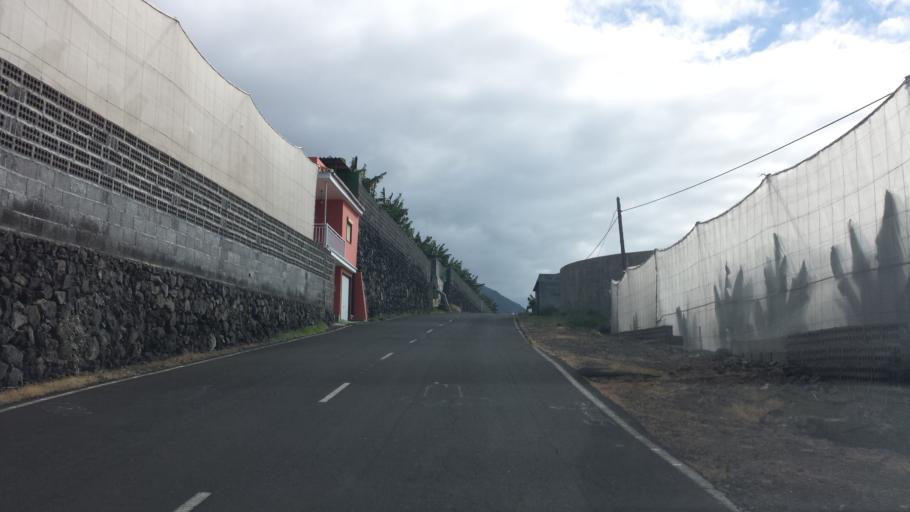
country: ES
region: Canary Islands
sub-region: Provincia de Santa Cruz de Tenerife
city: El Paso
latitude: 28.5663
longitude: -17.8930
